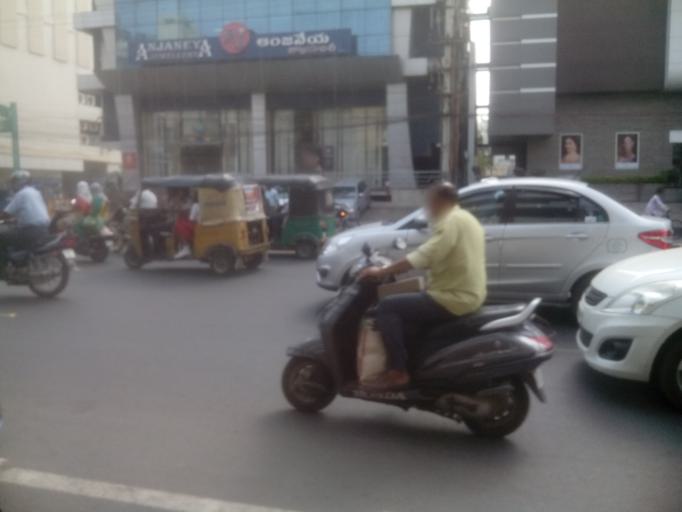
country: IN
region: Andhra Pradesh
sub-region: Krishna
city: Vijayawada
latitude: 16.5025
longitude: 80.6416
